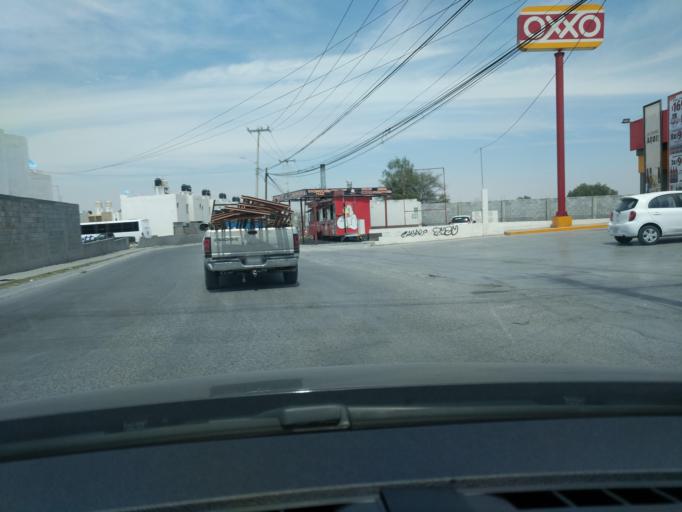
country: MX
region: Coahuila
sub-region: Arteaga
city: Arteaga
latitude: 25.4287
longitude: -100.9121
